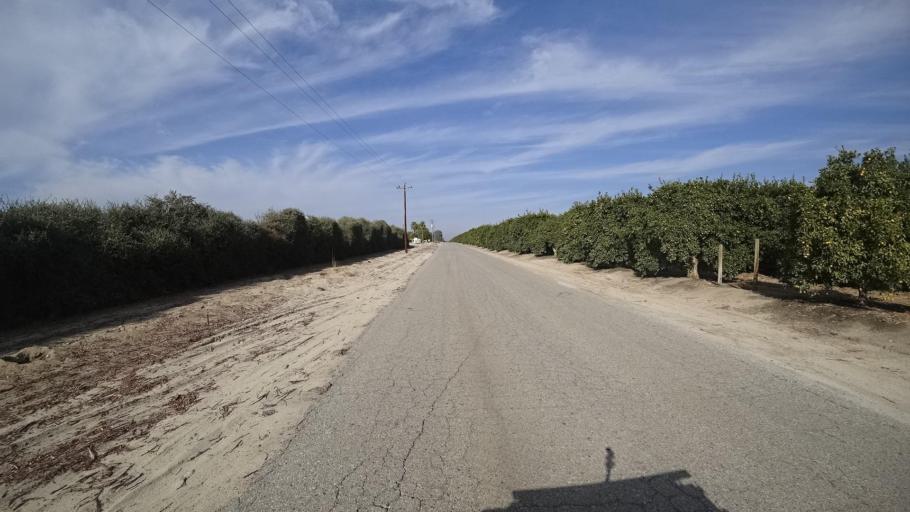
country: US
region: California
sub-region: Kern County
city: Arvin
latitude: 35.2752
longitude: -118.7527
